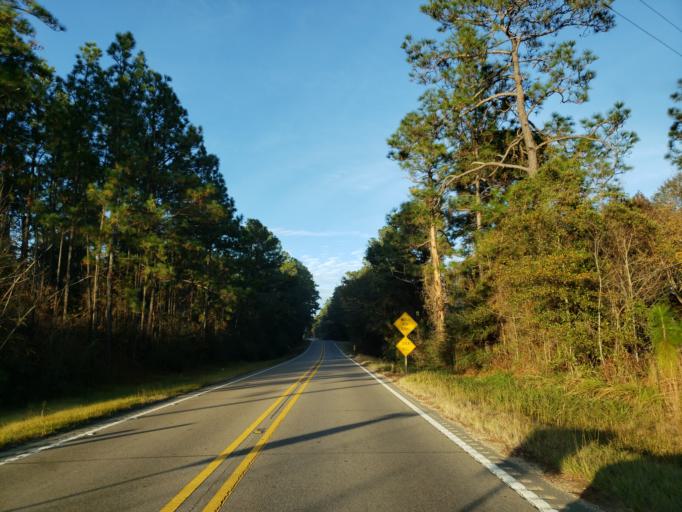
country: US
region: Mississippi
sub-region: Lamar County
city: Purvis
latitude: 31.1525
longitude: -89.3989
